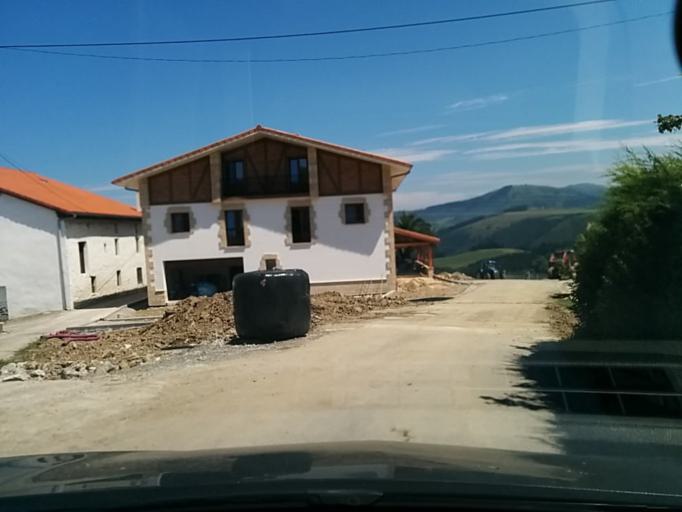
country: ES
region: Basque Country
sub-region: Provincia de Guipuzcoa
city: Zumaia
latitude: 43.2871
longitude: -2.2709
